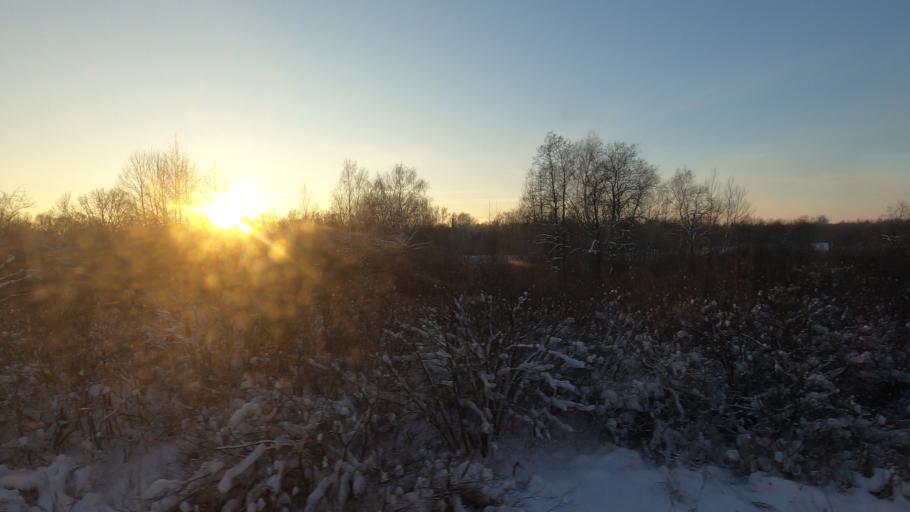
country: RU
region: Moskovskaya
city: Orud'yevo
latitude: 56.3981
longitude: 37.4951
